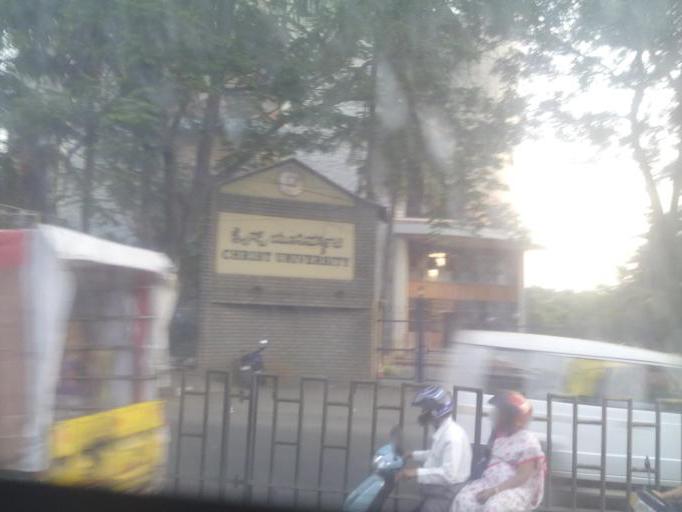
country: IN
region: Karnataka
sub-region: Bangalore Urban
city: Bangalore
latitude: 12.9366
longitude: 77.6043
